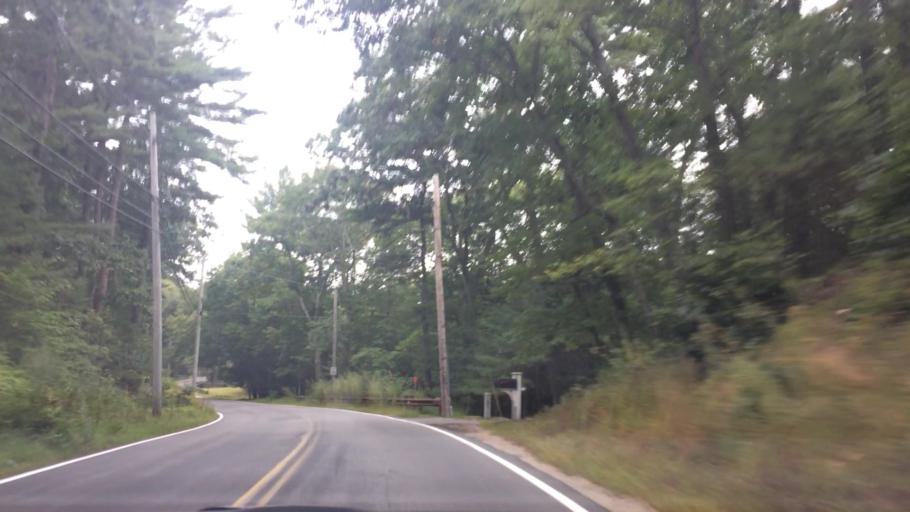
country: US
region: Massachusetts
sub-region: Essex County
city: Boxford
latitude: 42.6976
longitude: -71.0384
